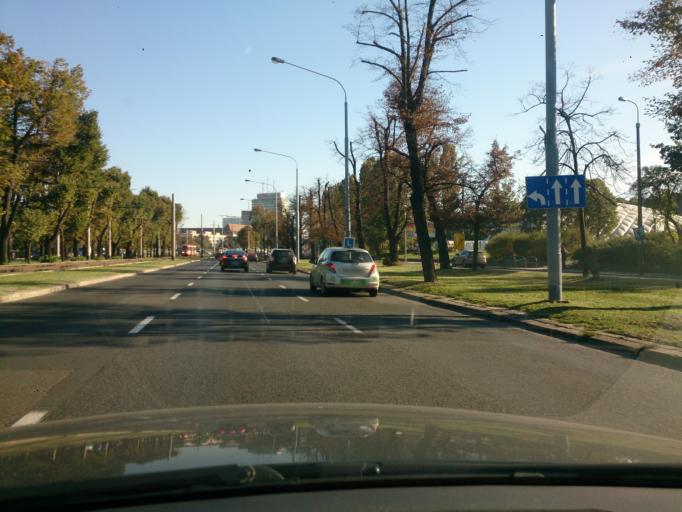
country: PL
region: Pomeranian Voivodeship
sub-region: Gdansk
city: Gdansk
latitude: 54.3634
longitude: 18.6393
